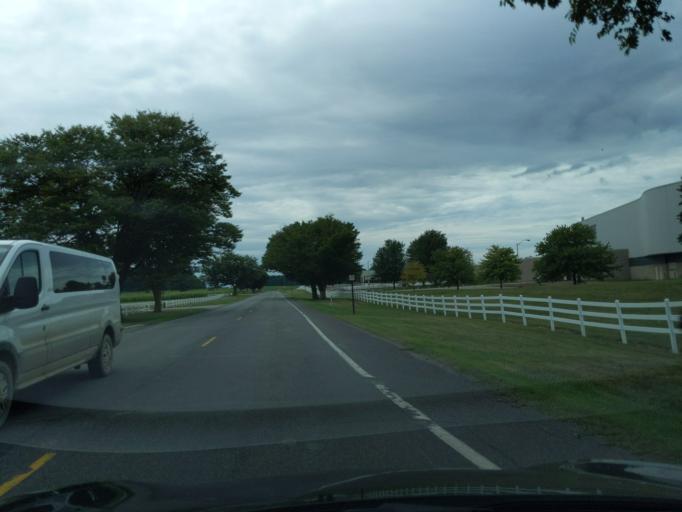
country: US
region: Michigan
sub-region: Ingham County
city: East Lansing
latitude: 42.7084
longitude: -84.4783
